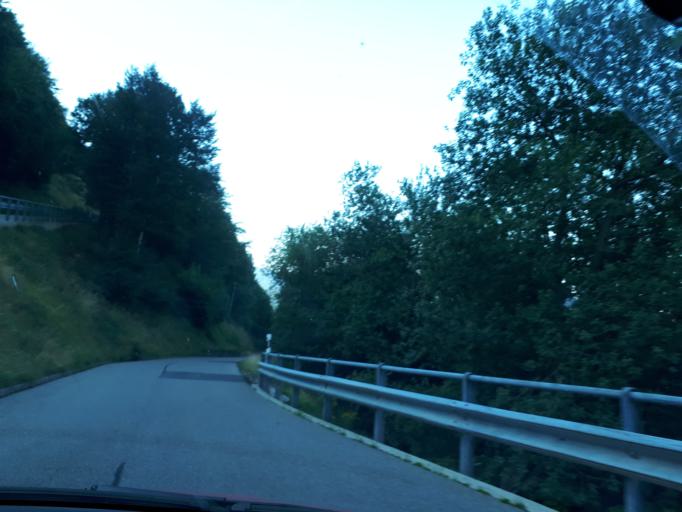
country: CH
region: Ticino
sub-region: Locarno District
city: Magadino
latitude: 46.1077
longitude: 8.8429
